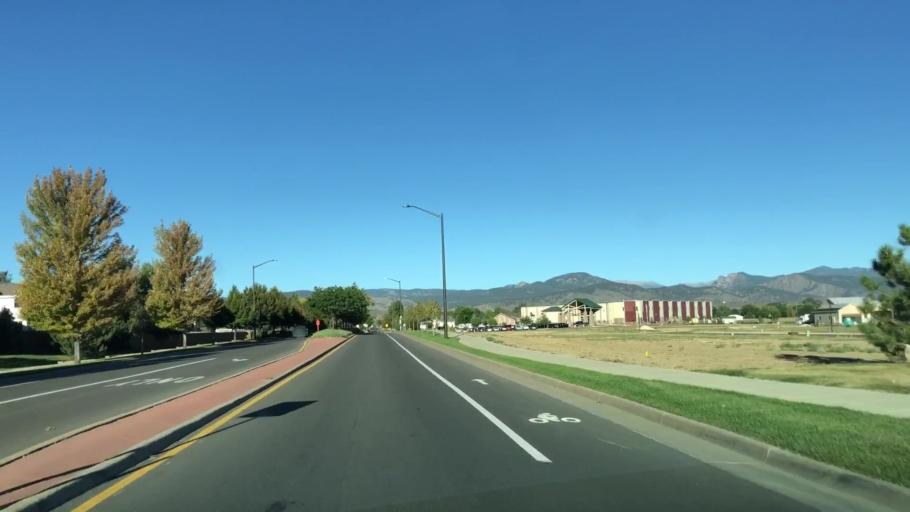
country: US
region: Colorado
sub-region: Larimer County
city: Loveland
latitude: 40.3785
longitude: -105.1260
